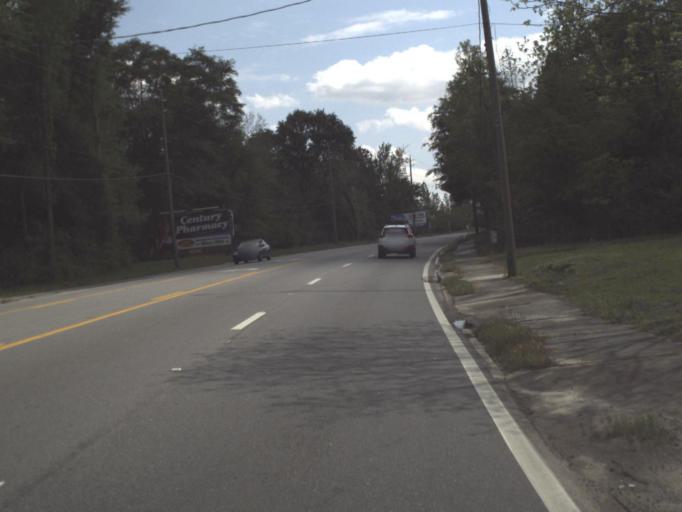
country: US
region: Alabama
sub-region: Escambia County
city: Flomaton
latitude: 30.9869
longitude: -87.2565
